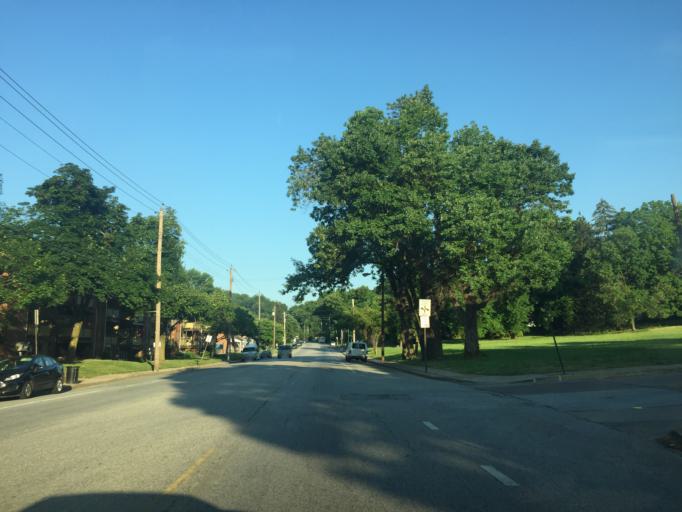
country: US
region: Maryland
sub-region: Baltimore County
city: Charlestown
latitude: 39.2814
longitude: -76.6955
